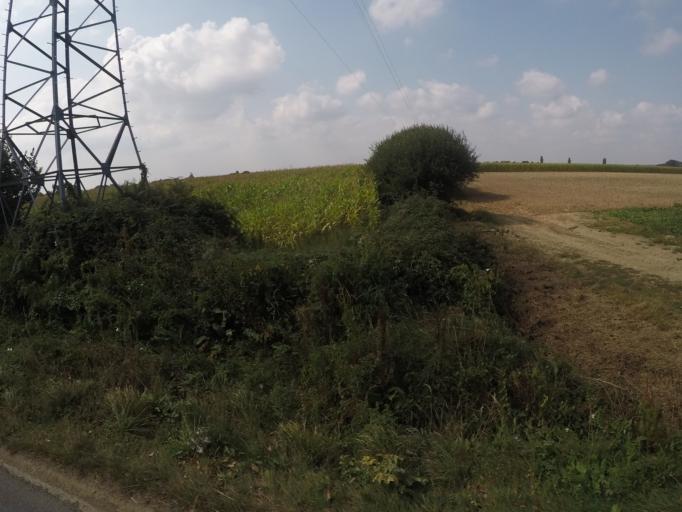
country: FR
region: Brittany
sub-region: Departement des Cotes-d'Armor
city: Lantic
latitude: 48.5561
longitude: -2.8918
